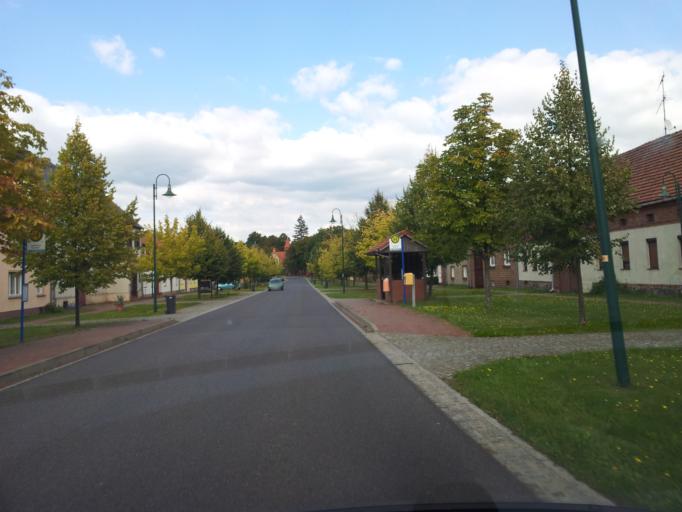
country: DE
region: Brandenburg
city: Sallgast
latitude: 51.5970
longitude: 13.7784
